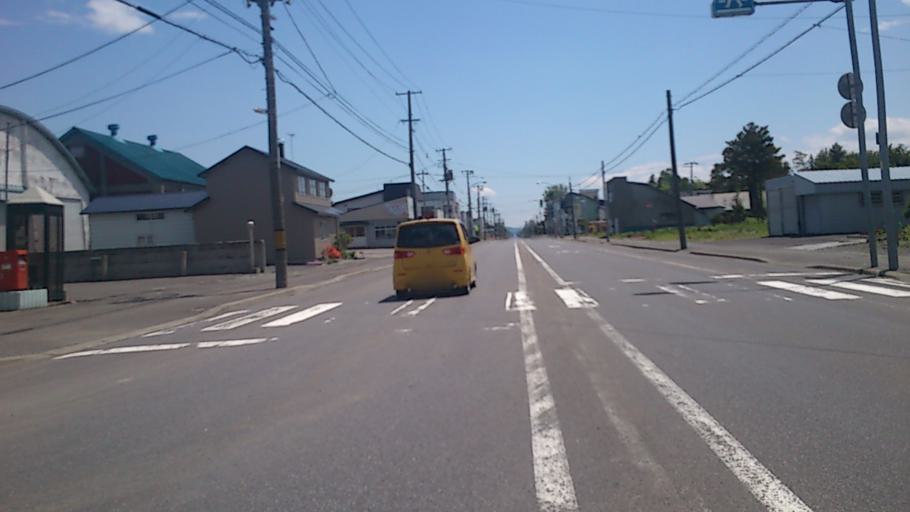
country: JP
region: Hokkaido
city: Nayoro
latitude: 44.2424
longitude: 142.3950
